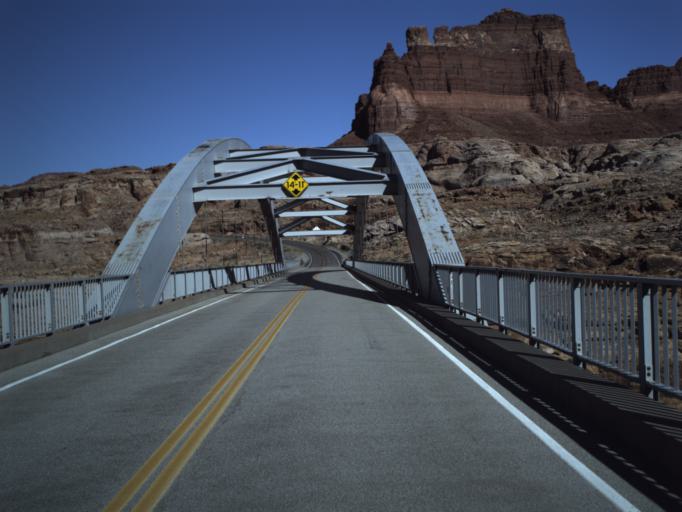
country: US
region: Utah
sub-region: San Juan County
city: Blanding
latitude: 37.8905
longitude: -110.3700
